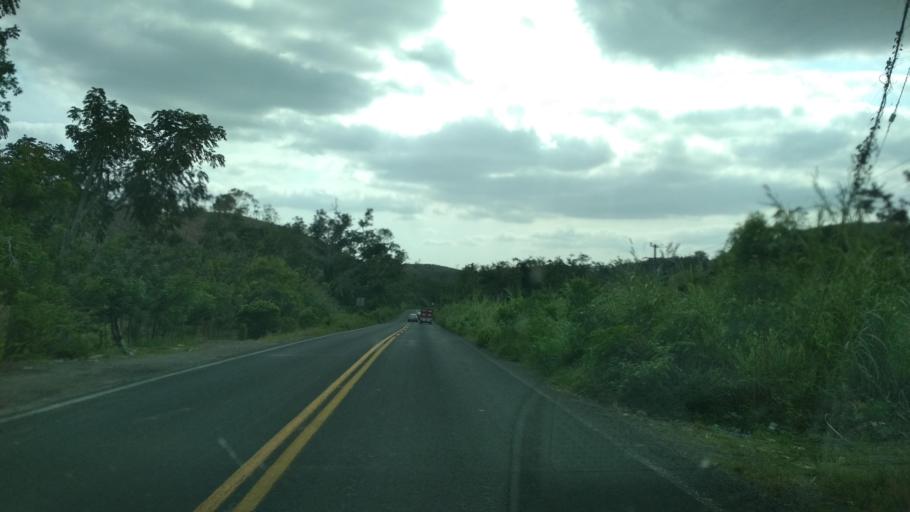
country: MX
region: Veracruz
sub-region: Papantla
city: Polutla
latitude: 20.4665
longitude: -97.2655
